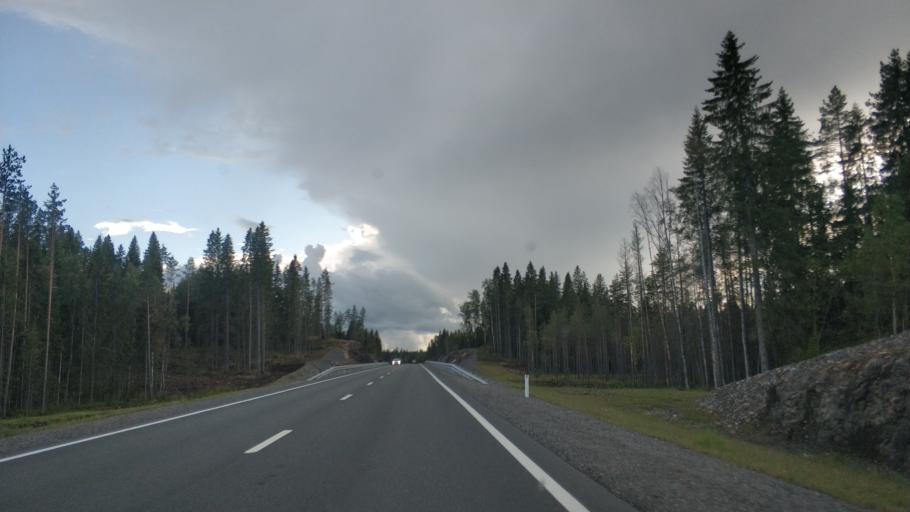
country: RU
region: Republic of Karelia
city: Lakhdenpokh'ya
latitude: 61.4343
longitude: 29.9765
